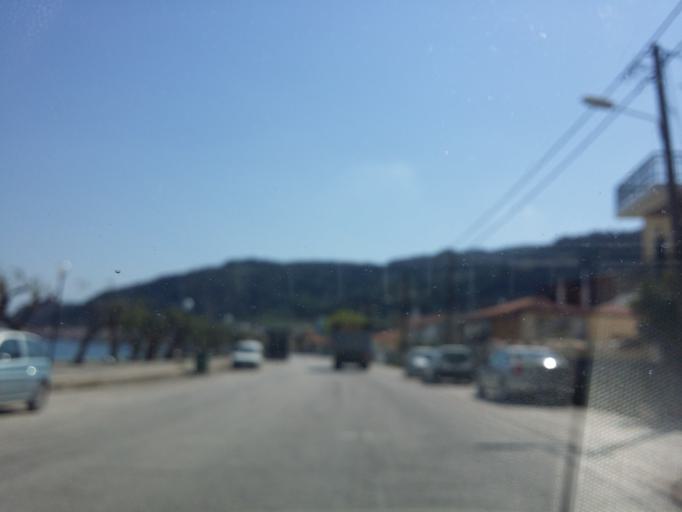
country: GR
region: West Greece
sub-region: Nomos Achaias
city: Aiyira
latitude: 38.1318
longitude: 22.4090
